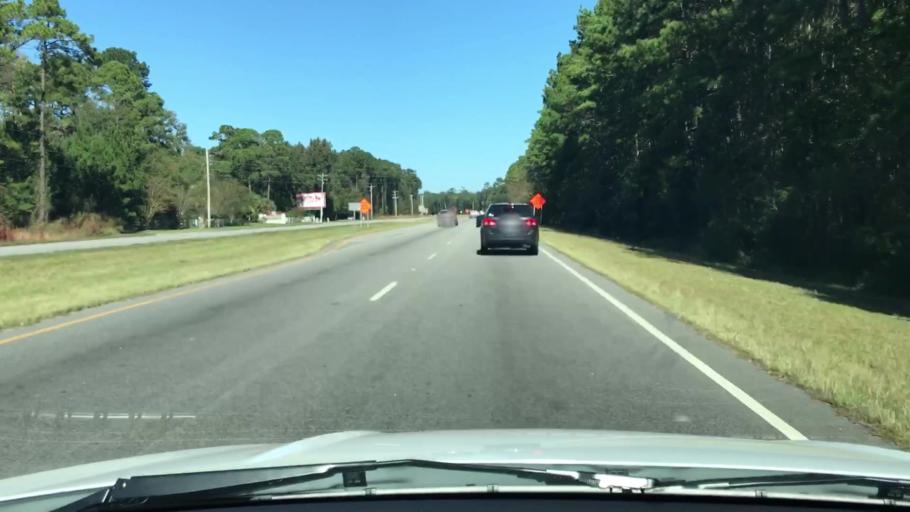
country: US
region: South Carolina
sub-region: Beaufort County
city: Bluffton
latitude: 32.3258
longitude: -80.9313
